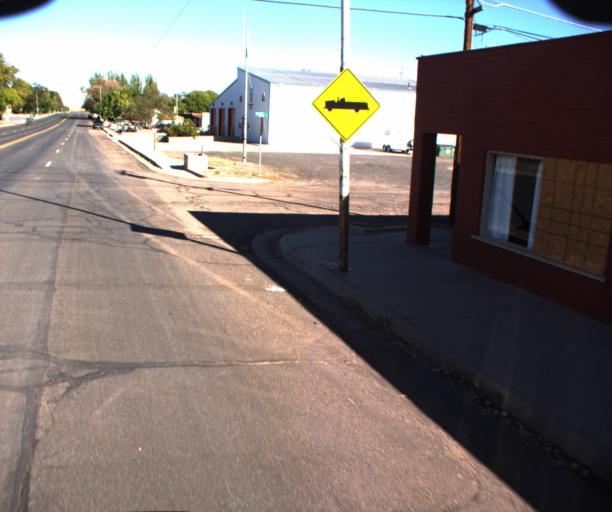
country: US
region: Arizona
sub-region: Navajo County
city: Joseph City
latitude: 34.9560
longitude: -110.3348
